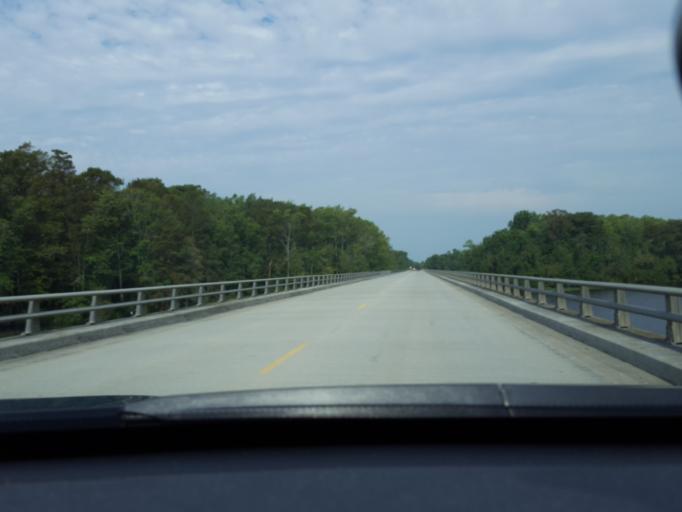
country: US
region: North Carolina
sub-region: Washington County
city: Plymouth
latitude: 35.9200
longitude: -76.7289
